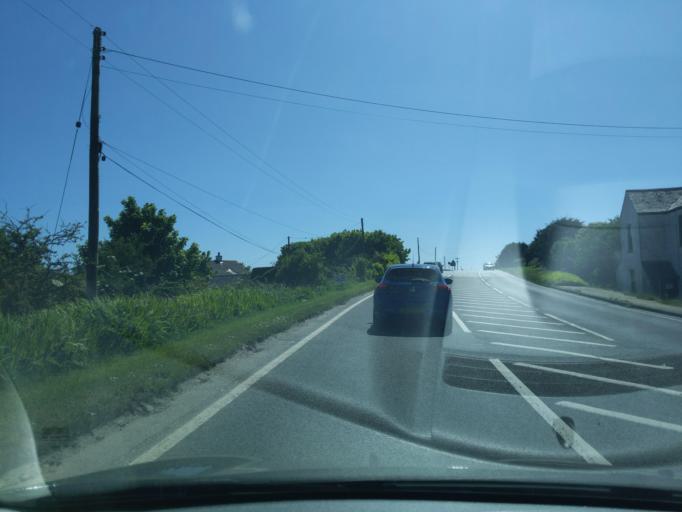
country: GB
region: England
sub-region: Cornwall
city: Wendron
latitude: 50.1531
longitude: -5.1940
